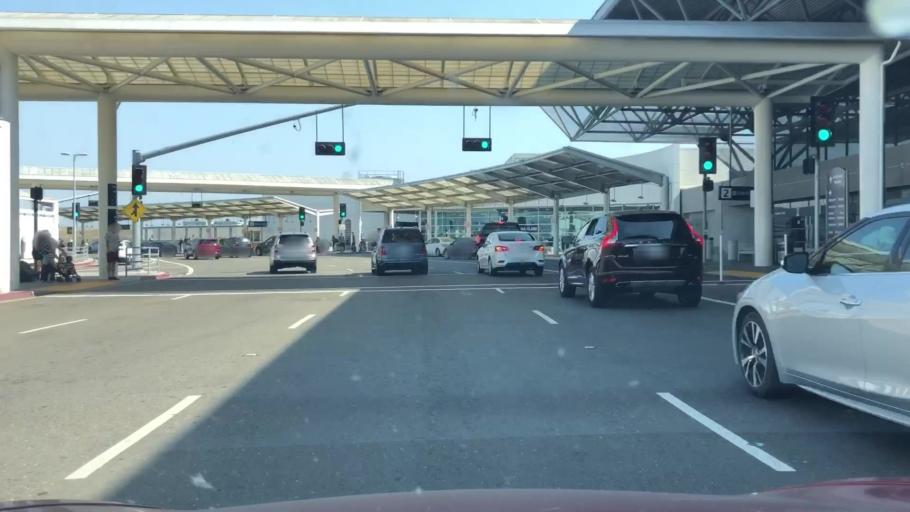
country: US
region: California
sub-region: Alameda County
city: San Leandro
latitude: 37.7118
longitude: -122.2119
